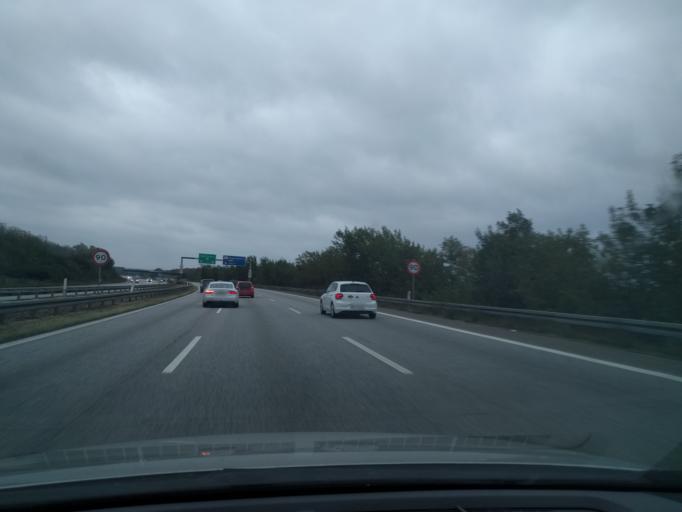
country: DK
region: Capital Region
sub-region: Frederiksberg Kommune
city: Frederiksberg
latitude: 55.6284
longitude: 12.5187
